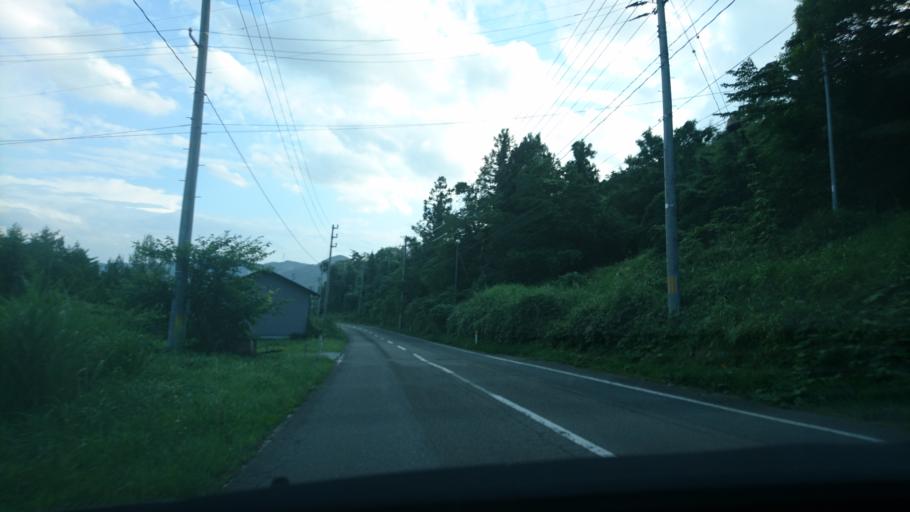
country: JP
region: Iwate
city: Ichinoseki
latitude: 39.0071
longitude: 141.2848
